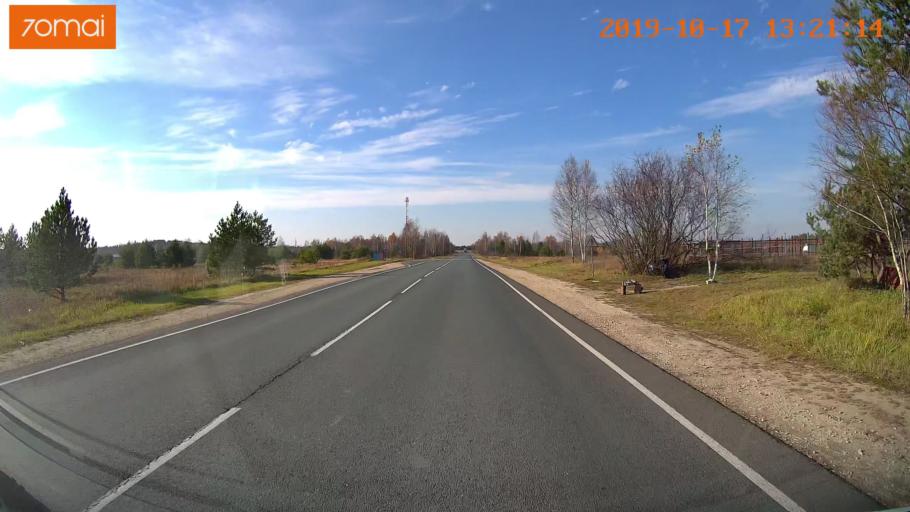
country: RU
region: Rjazan
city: Gus'-Zheleznyy
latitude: 55.0802
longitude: 41.0320
